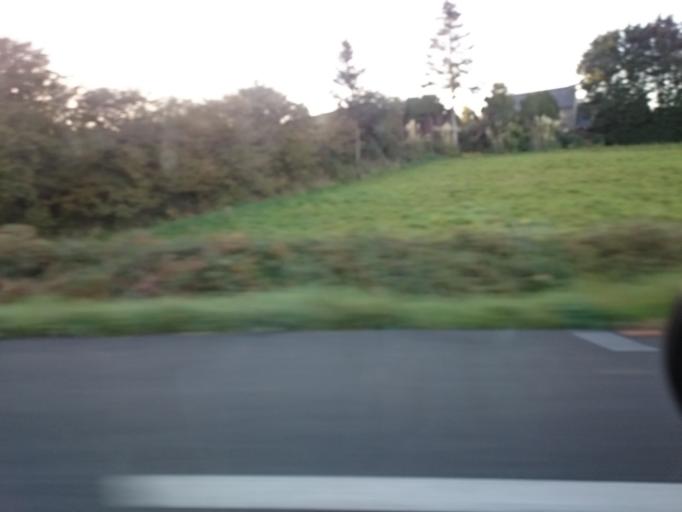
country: FR
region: Brittany
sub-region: Departement du Finistere
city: Morlaix
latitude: 48.5844
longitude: -3.8502
